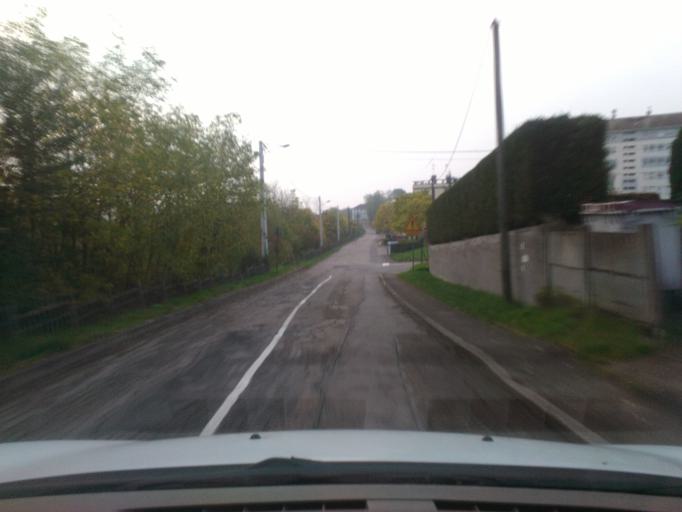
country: FR
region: Lorraine
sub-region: Departement des Vosges
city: Mirecourt
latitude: 48.3028
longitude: 6.1277
